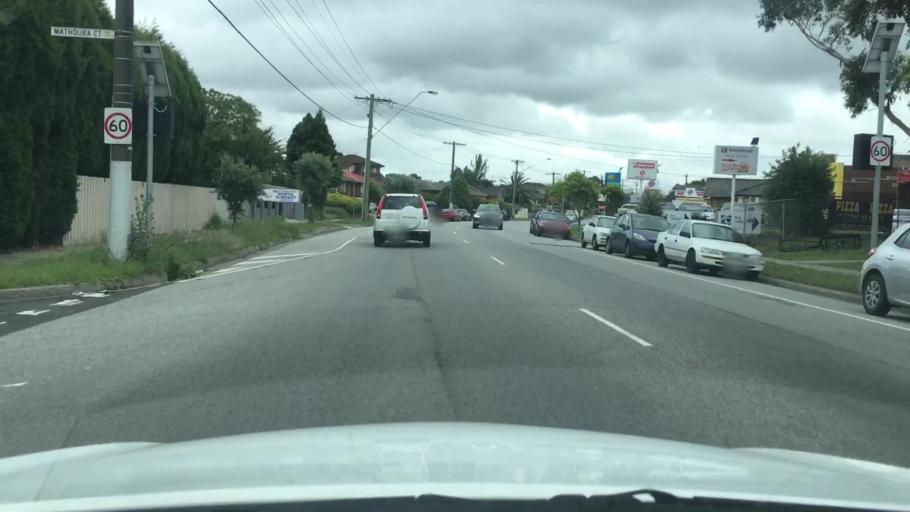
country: AU
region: Victoria
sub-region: Greater Dandenong
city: Noble Park North
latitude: -37.9471
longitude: 145.1917
